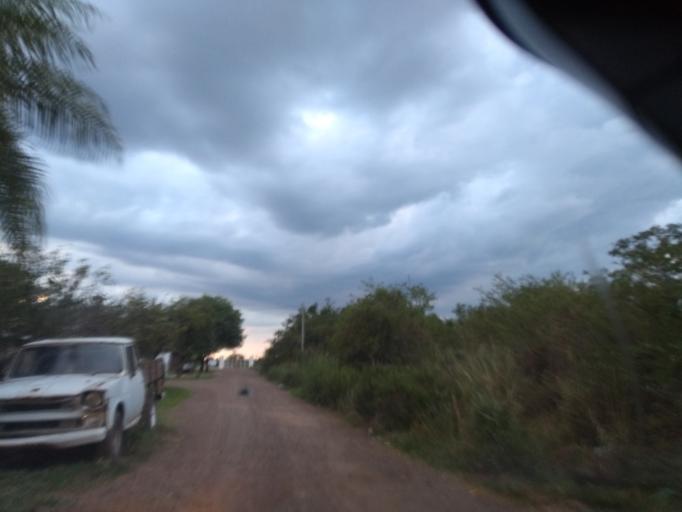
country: AR
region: Chaco
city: Fontana
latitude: -27.4120
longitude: -59.0362
